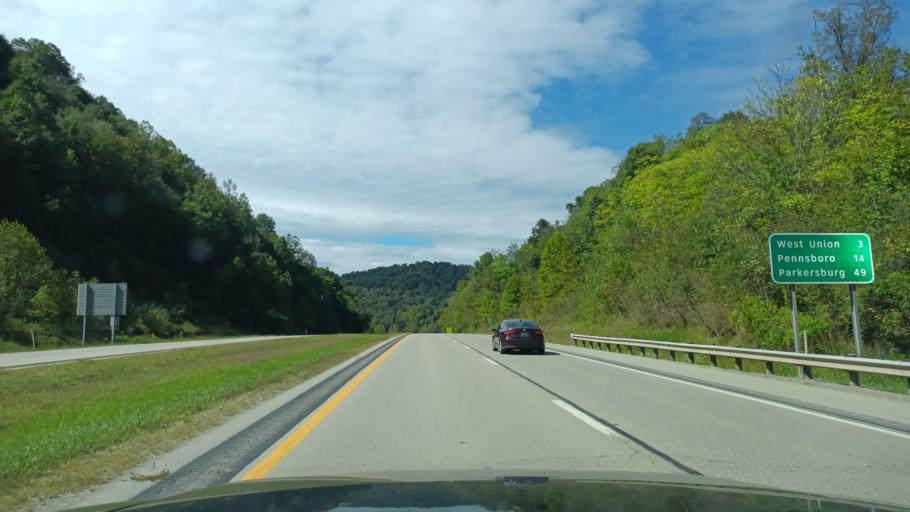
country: US
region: West Virginia
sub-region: Doddridge County
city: West Union
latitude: 39.2875
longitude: -80.7353
